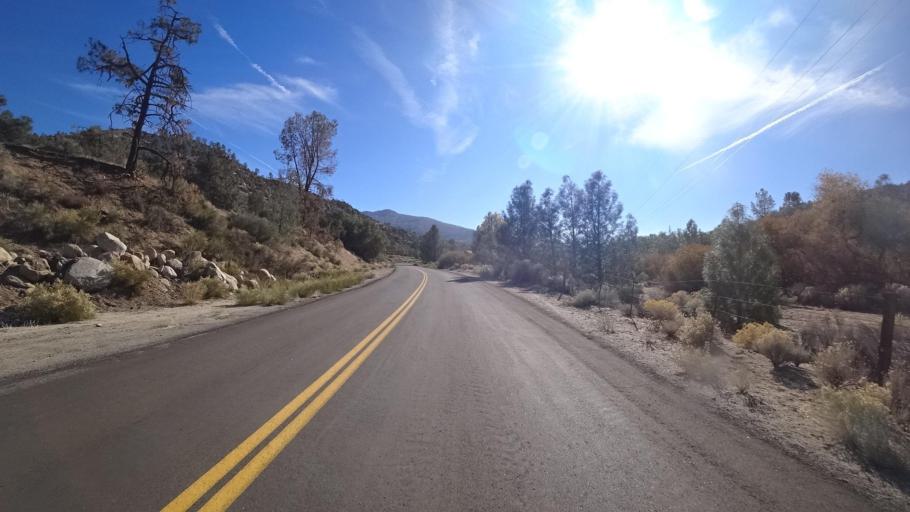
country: US
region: California
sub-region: Kern County
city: Bodfish
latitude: 35.5281
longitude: -118.5121
